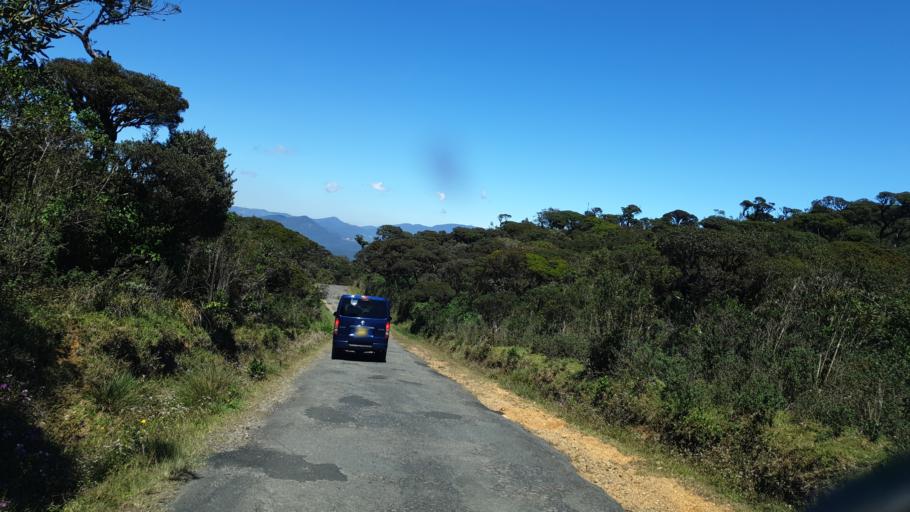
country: LK
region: Central
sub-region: Nuwara Eliya District
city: Nuwara Eliya
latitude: 6.8409
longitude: 80.8127
